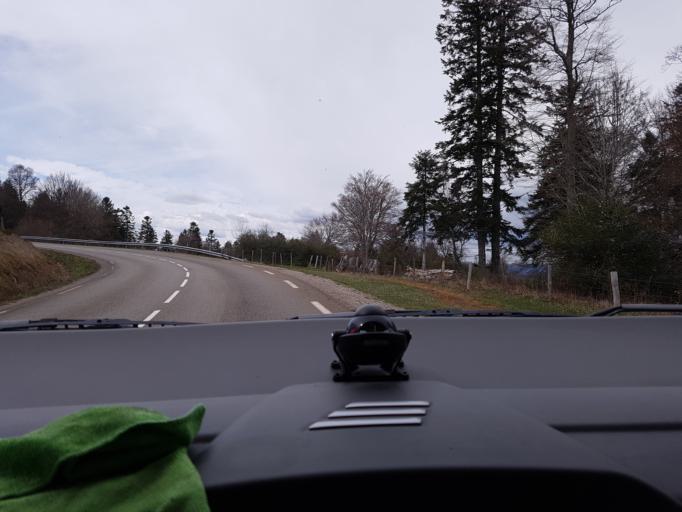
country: FR
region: Midi-Pyrenees
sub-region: Departement de l'Aveyron
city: Laguiole
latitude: 44.7786
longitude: 2.8980
